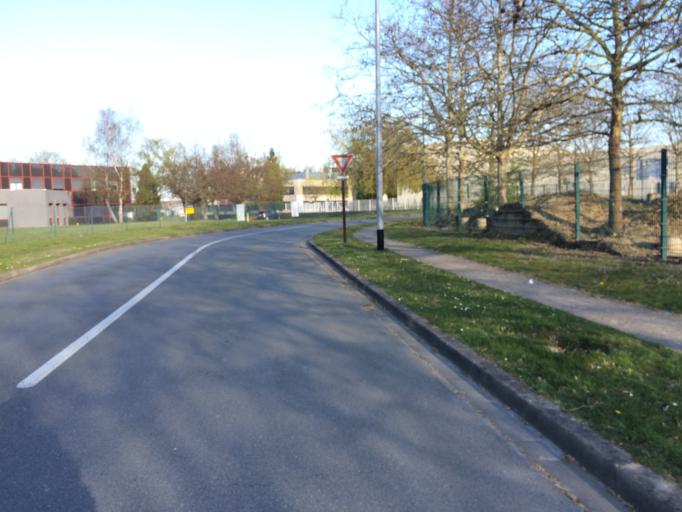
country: FR
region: Ile-de-France
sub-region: Departement de l'Essonne
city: Villejust
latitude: 48.6924
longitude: 2.2151
